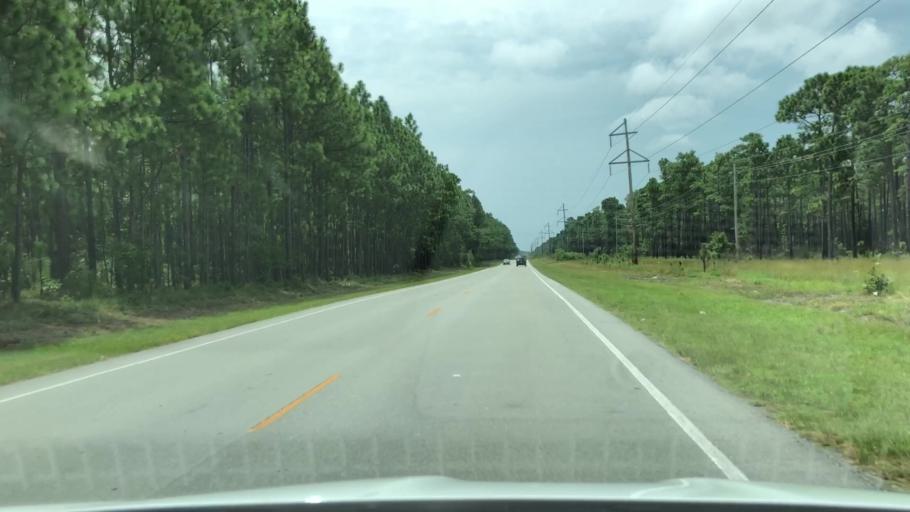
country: US
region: North Carolina
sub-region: Carteret County
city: Newport
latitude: 34.7642
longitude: -76.8691
